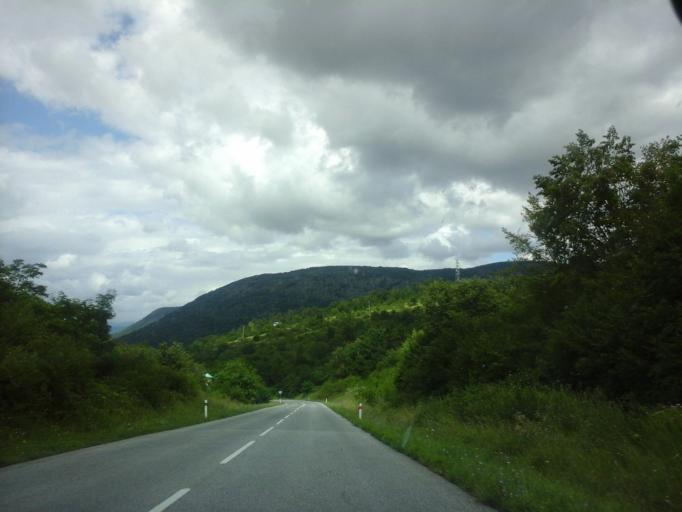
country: SK
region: Kosicky
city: Roznava
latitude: 48.5402
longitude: 20.4080
